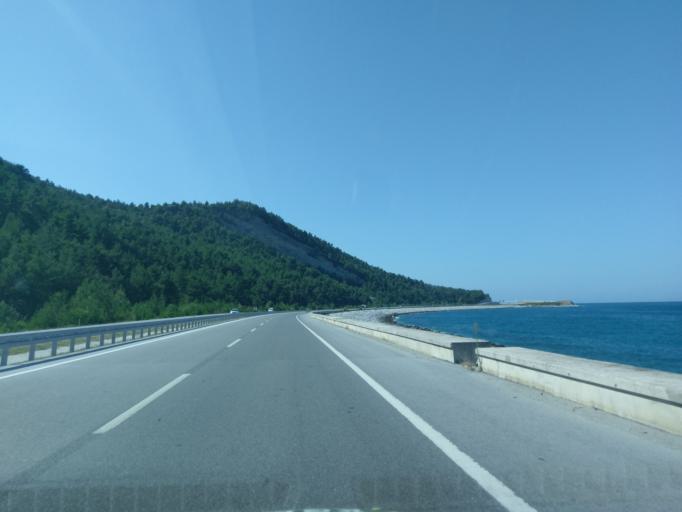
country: TR
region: Samsun
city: Yakakent
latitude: 41.6719
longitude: 35.4250
